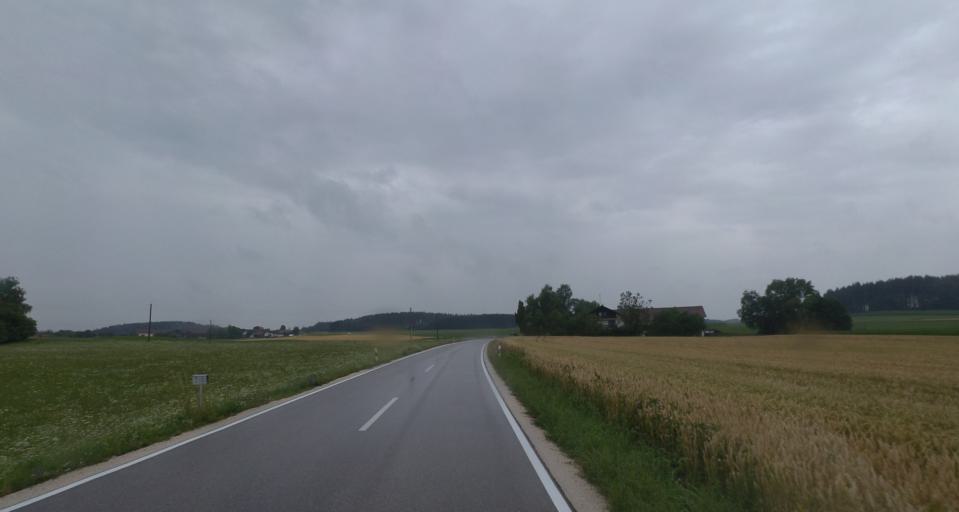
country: DE
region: Bavaria
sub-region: Upper Bavaria
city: Traunreut
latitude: 47.9502
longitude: 12.5527
